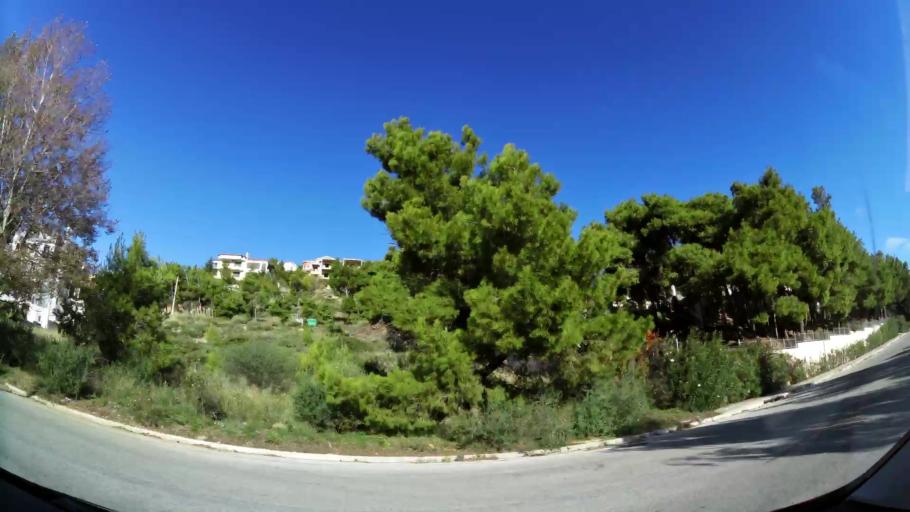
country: GR
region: Attica
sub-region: Nomarchia Anatolikis Attikis
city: Dhrafi
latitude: 38.0222
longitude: 23.9089
